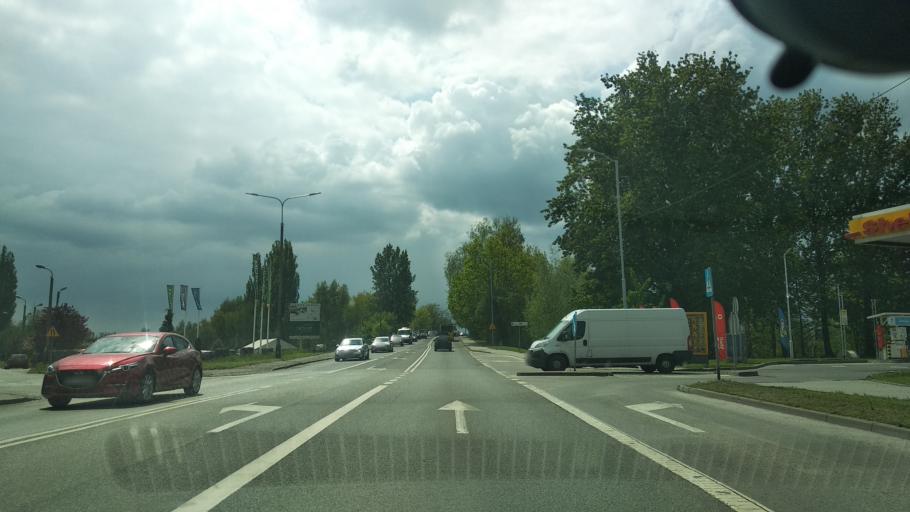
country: PL
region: Silesian Voivodeship
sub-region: Katowice
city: Katowice
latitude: 50.2334
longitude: 18.9760
